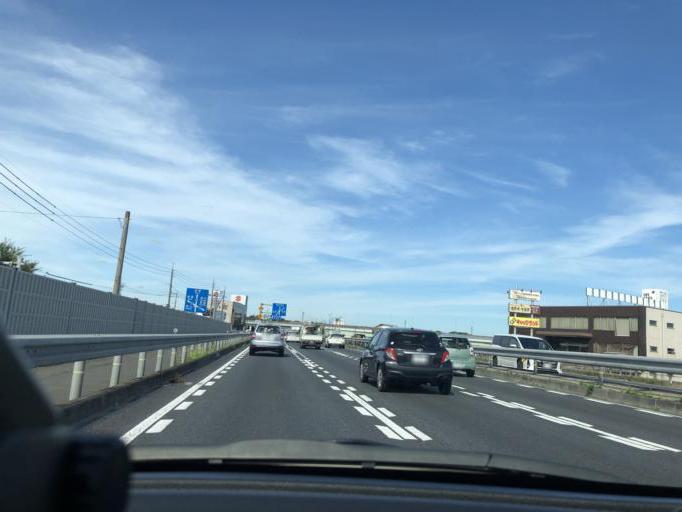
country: JP
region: Okayama
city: Kurashiki
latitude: 34.5972
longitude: 133.8081
